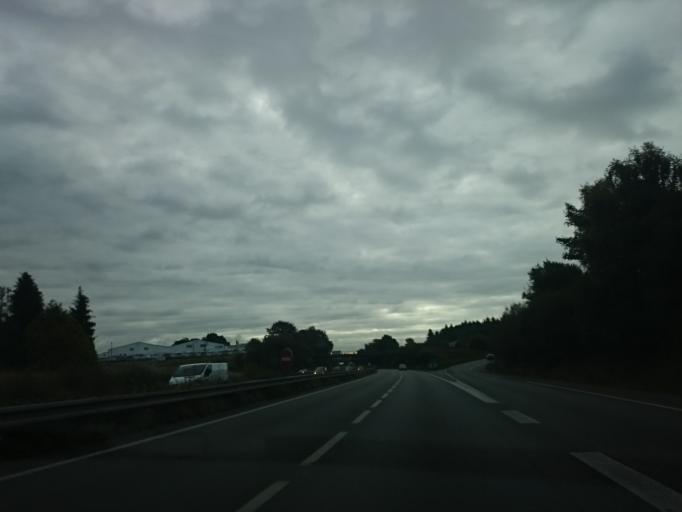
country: FR
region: Brittany
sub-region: Departement du Morbihan
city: Queven
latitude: 47.7796
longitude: -3.4219
